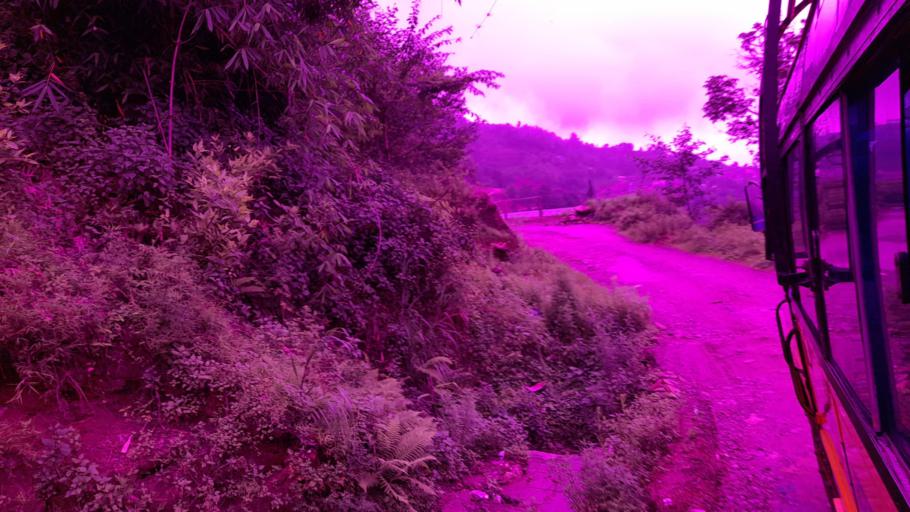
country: NP
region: Central Region
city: Kirtipur
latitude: 27.8172
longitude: 85.2138
